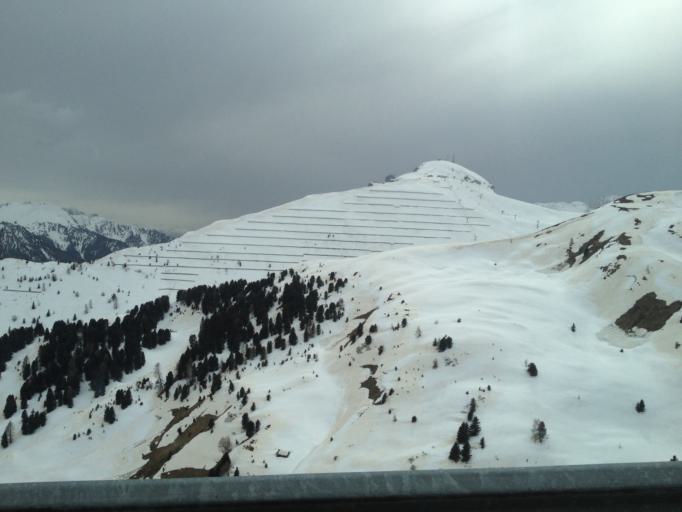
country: IT
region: Trentino-Alto Adige
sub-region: Provincia di Trento
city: Canazei
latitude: 46.5061
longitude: 11.7711
